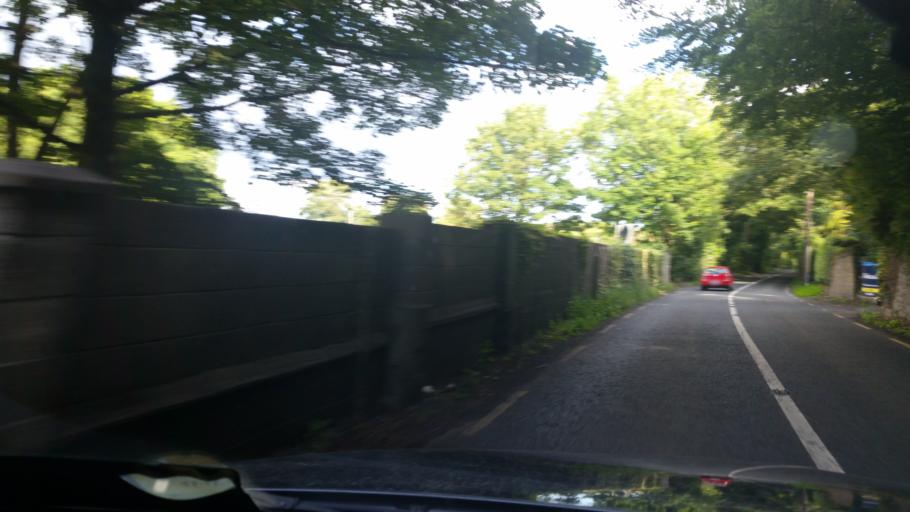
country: IE
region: Leinster
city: Castleknock
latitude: 53.3803
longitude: -6.3451
